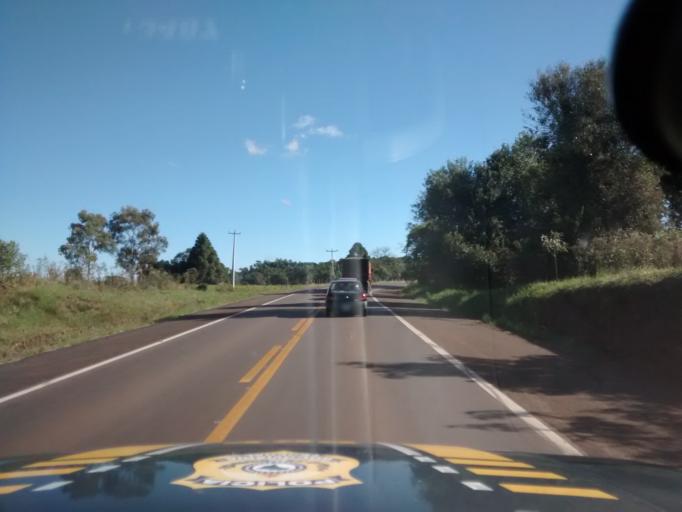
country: BR
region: Rio Grande do Sul
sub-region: Lagoa Vermelha
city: Lagoa Vermelha
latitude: -28.2979
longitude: -51.4501
